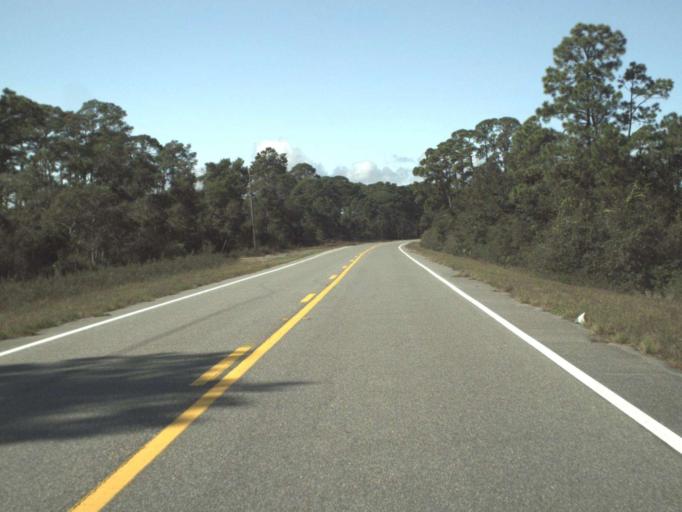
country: US
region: Florida
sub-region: Franklin County
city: Carrabelle
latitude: 29.9268
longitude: -84.4278
